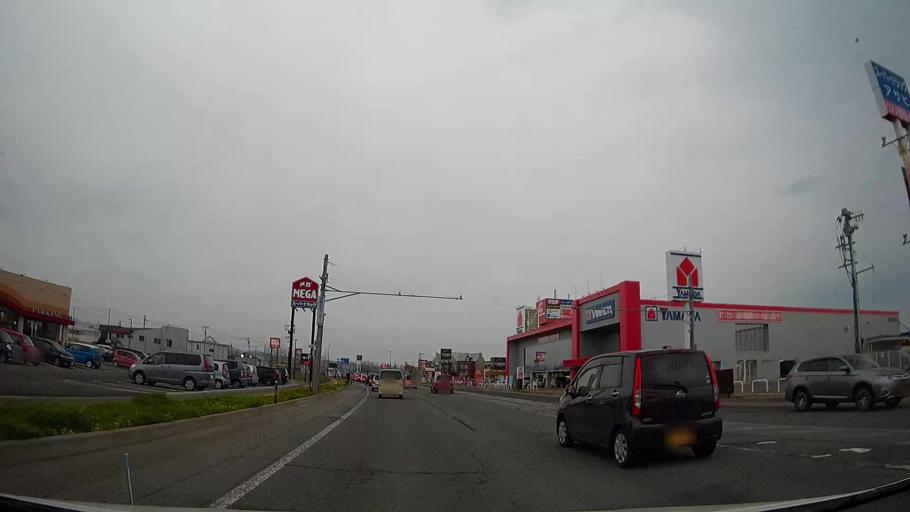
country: JP
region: Aomori
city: Aomori Shi
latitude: 40.8311
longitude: 140.7035
